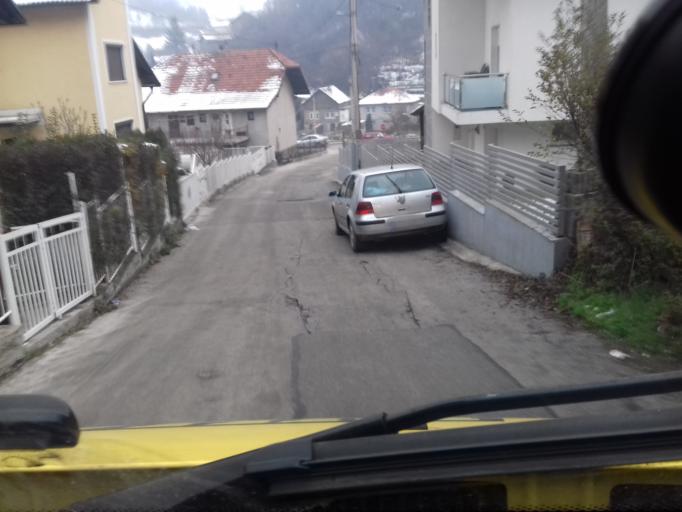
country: BA
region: Federation of Bosnia and Herzegovina
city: Zenica
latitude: 44.1970
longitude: 17.8946
